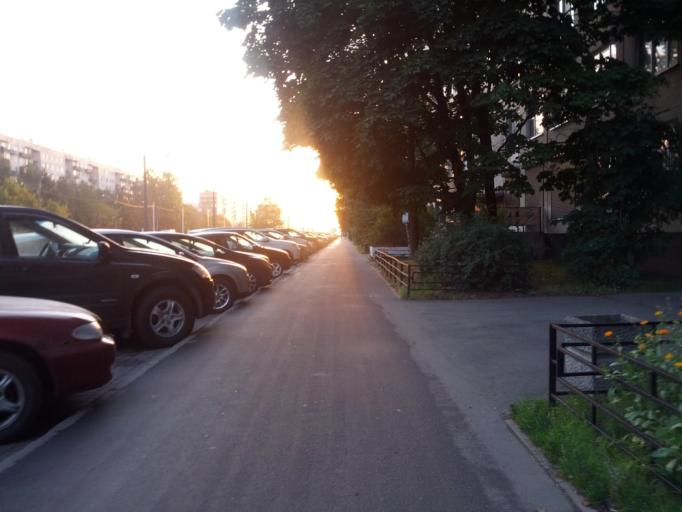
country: RU
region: St.-Petersburg
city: Obukhovo
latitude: 59.9041
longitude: 30.4726
